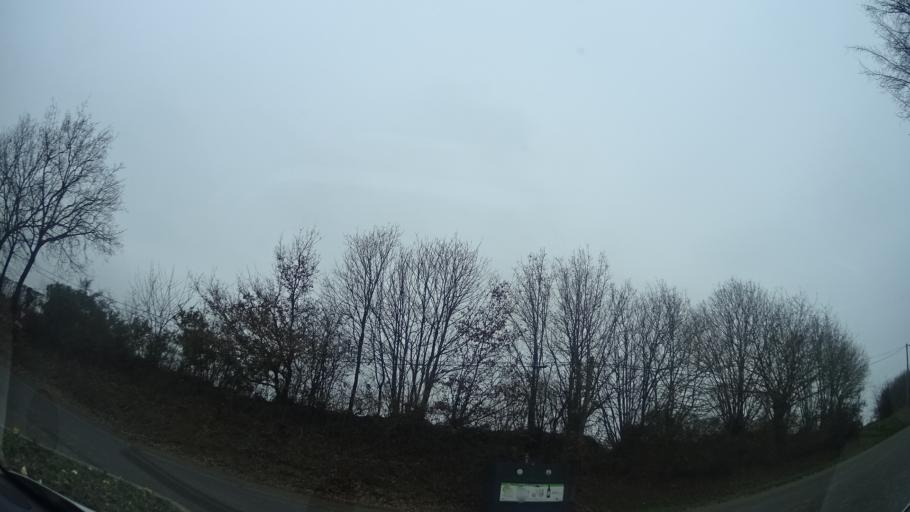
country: FR
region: Brittany
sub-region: Departement d'Ille-et-Vilaine
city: Brece
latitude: 48.1103
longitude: -1.4785
